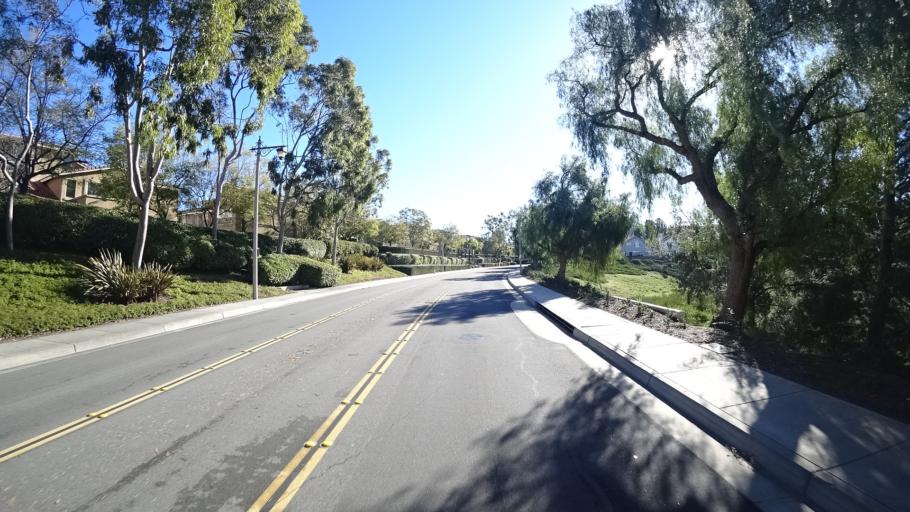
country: US
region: California
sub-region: Orange County
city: Villa Park
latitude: 33.8514
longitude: -117.7437
